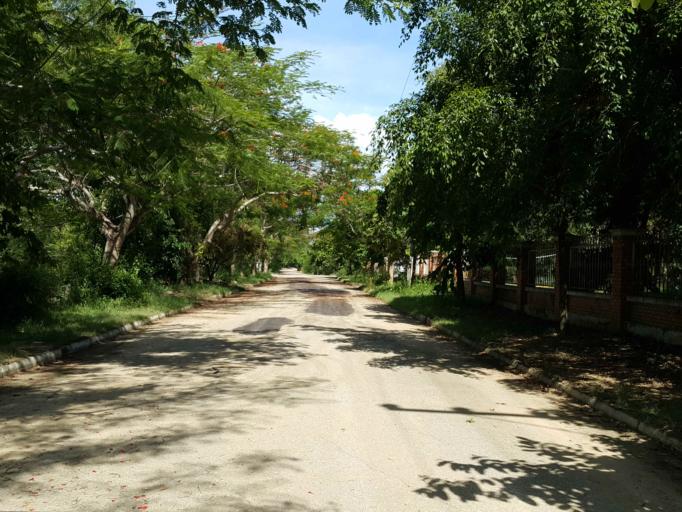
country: TH
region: Chiang Mai
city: San Kamphaeng
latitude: 18.7601
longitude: 99.1129
